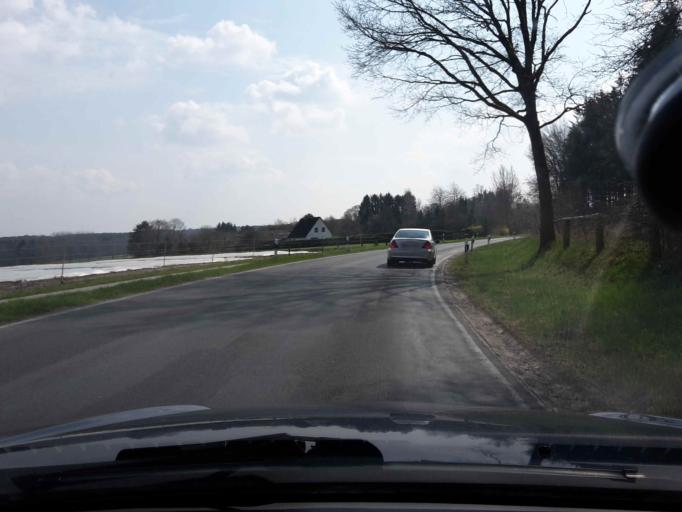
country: DE
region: Lower Saxony
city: Buchholz in der Nordheide
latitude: 53.3194
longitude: 9.8949
